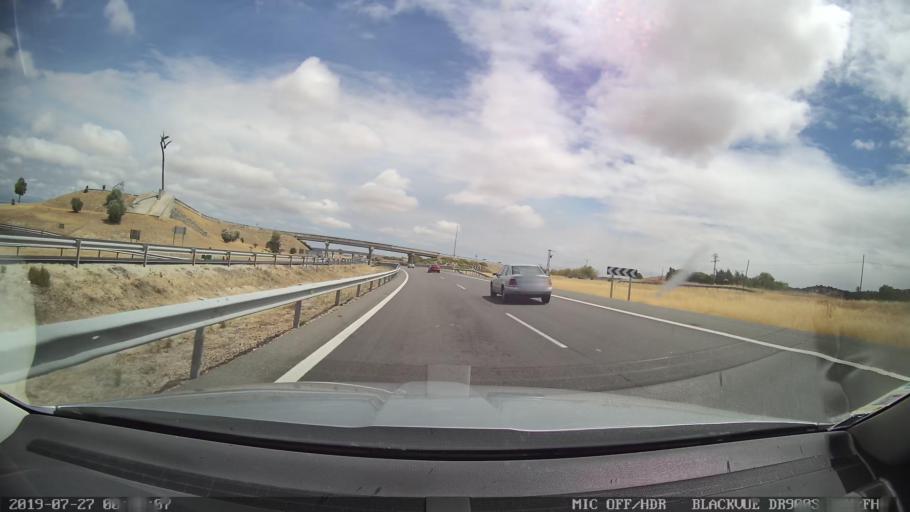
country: ES
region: Castille-La Mancha
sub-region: Province of Toledo
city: Lagartera
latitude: 39.9078
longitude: -5.2146
